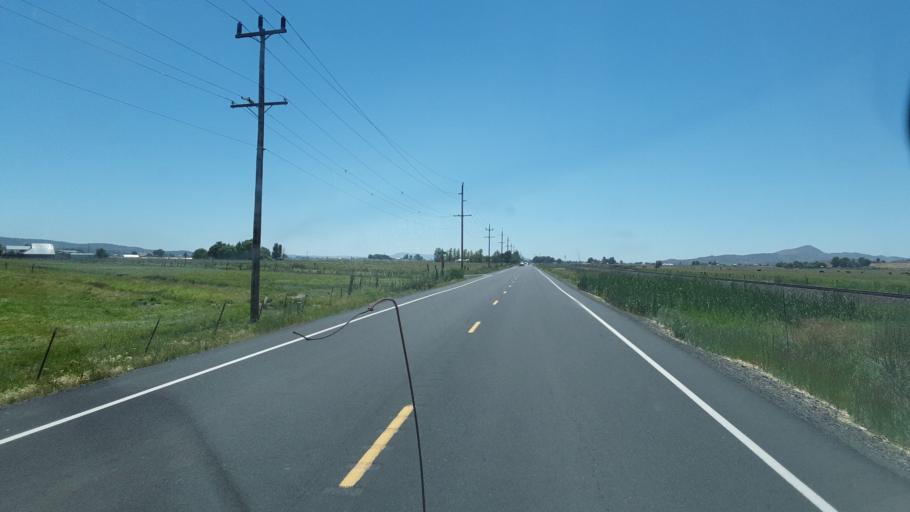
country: US
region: Oregon
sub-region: Klamath County
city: Altamont
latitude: 42.0575
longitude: -121.6476
